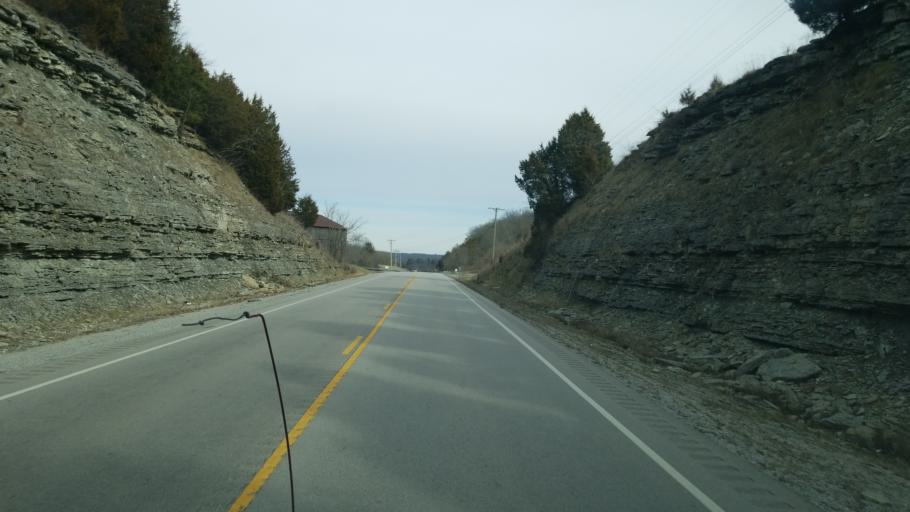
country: US
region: Kentucky
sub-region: Nicholas County
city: Carlisle
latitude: 38.4144
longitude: -84.0048
